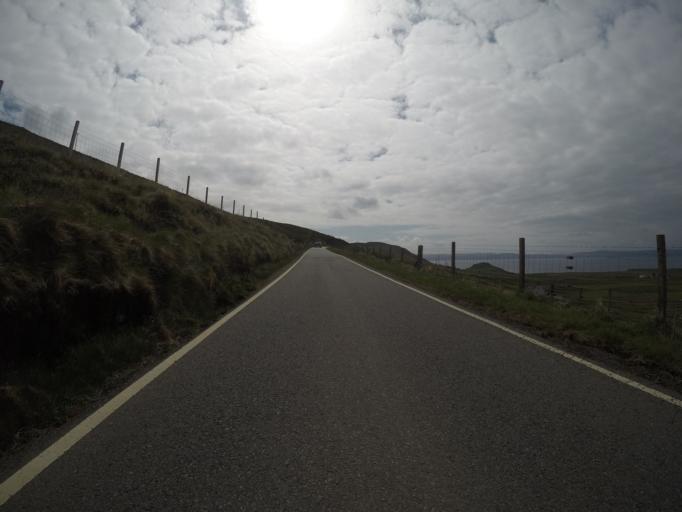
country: GB
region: Scotland
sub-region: Highland
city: Portree
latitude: 57.6068
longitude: -6.3748
